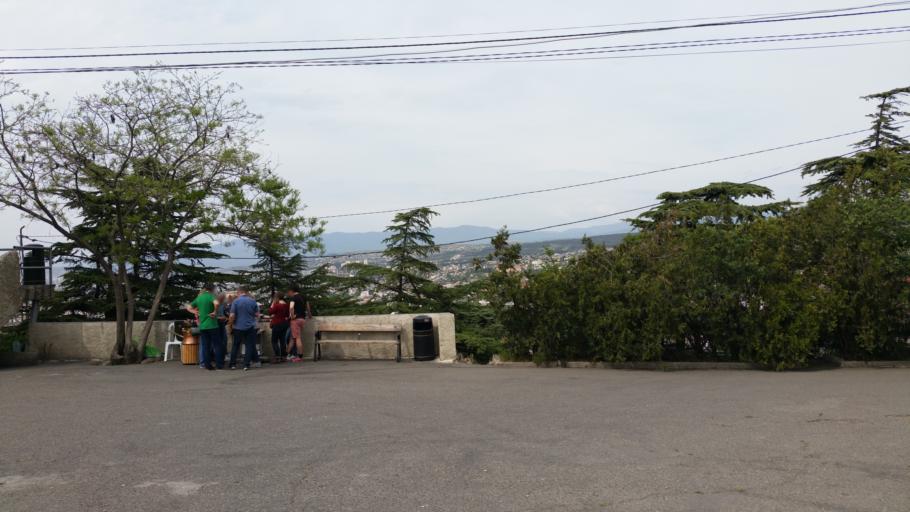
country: GE
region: T'bilisi
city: Tbilisi
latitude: 41.6880
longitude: 44.8048
